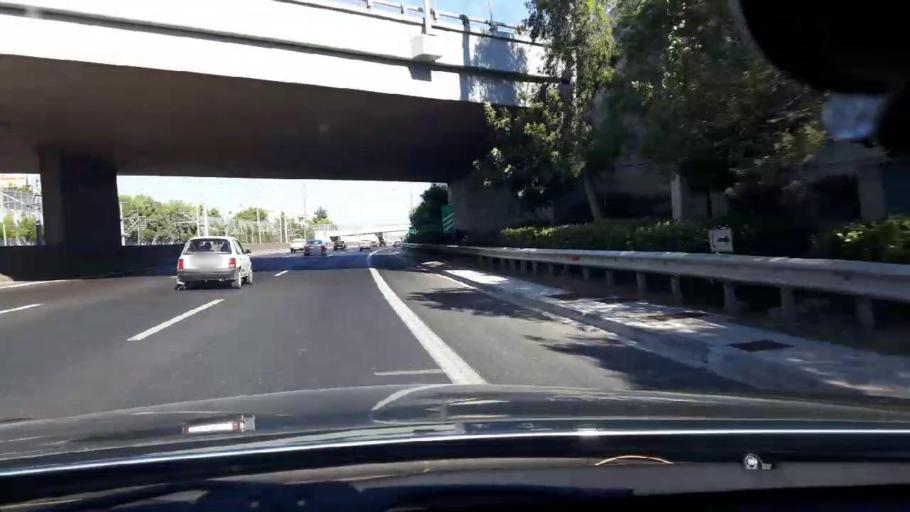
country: GR
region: Attica
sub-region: Nomarchia Anatolikis Attikis
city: Gerakas
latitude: 38.0115
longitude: 23.8679
